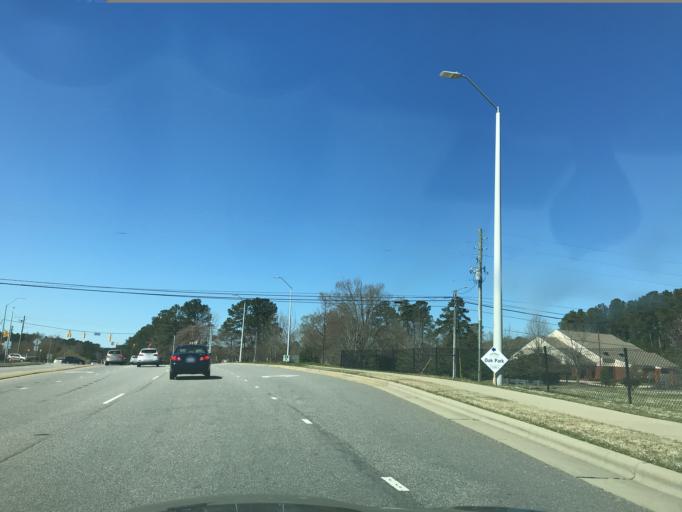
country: US
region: North Carolina
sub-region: Wake County
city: Garner
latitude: 35.6863
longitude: -78.6024
